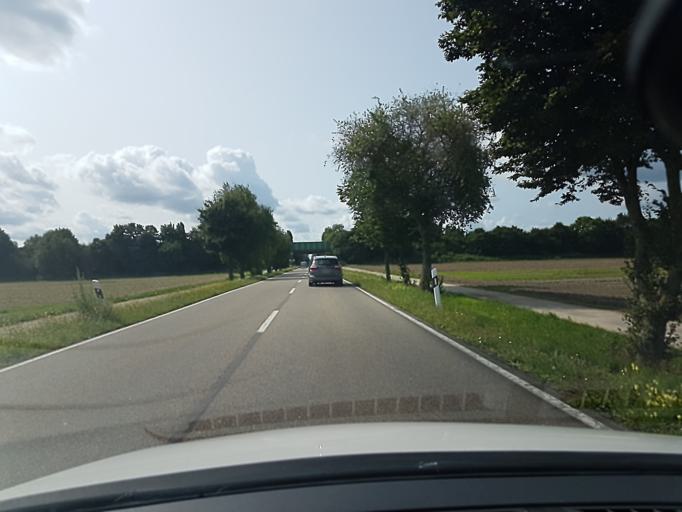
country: DE
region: Rheinland-Pfalz
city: Otterstadt
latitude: 49.3553
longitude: 8.4352
